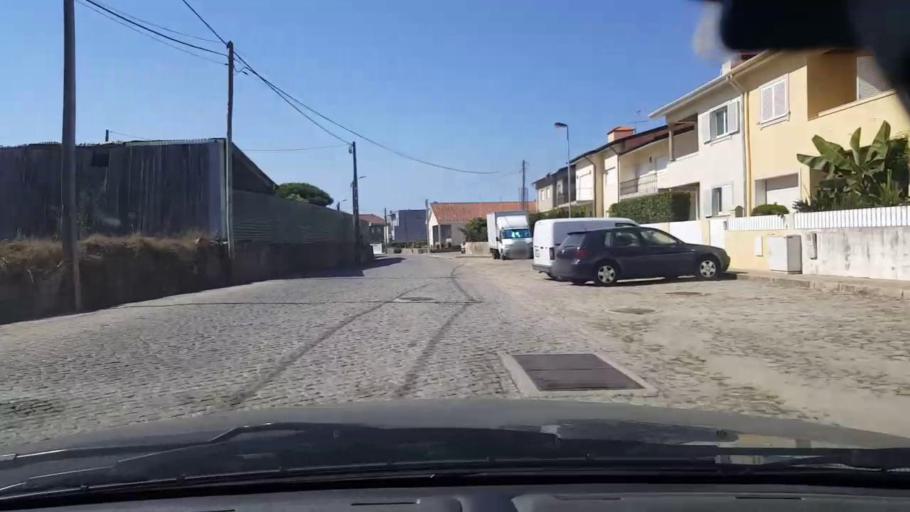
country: PT
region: Porto
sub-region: Matosinhos
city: Lavra
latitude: 41.2944
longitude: -8.7169
